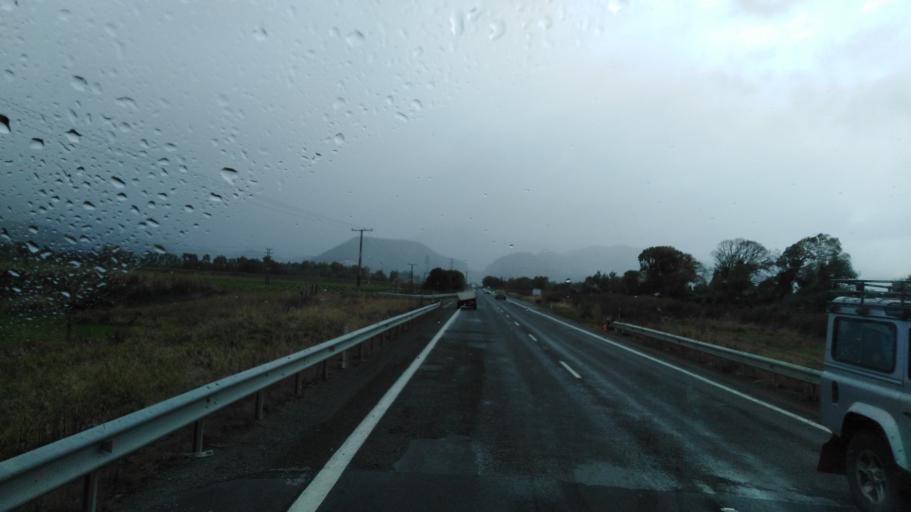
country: NZ
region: Marlborough
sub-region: Marlborough District
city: Blenheim
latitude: -41.4460
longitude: 173.9651
